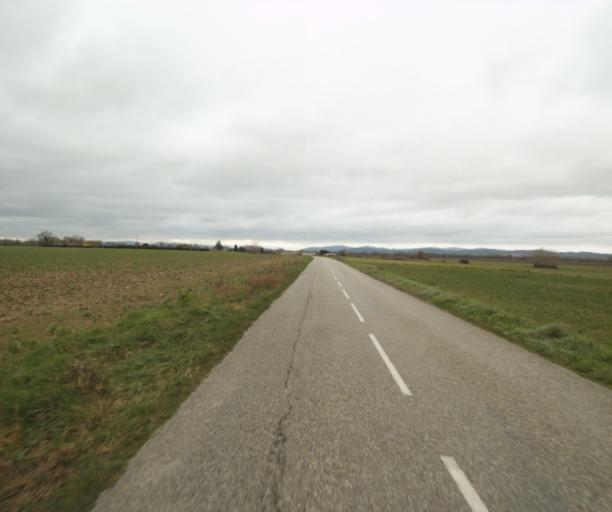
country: FR
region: Midi-Pyrenees
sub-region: Departement de l'Ariege
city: Pamiers
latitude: 43.1722
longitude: 1.6356
